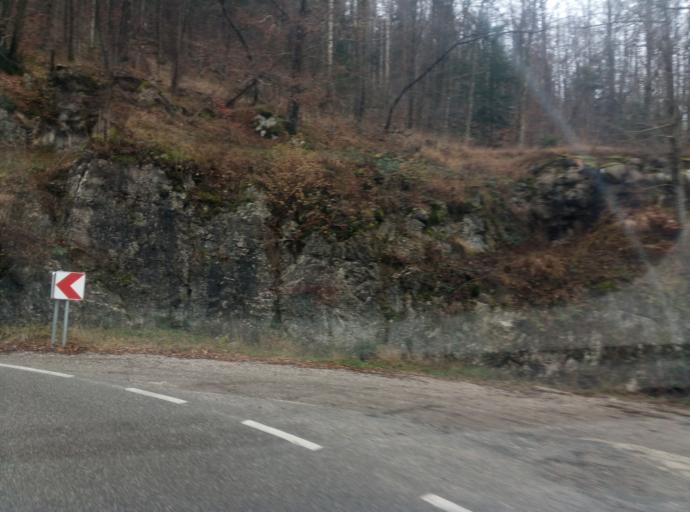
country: SI
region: Idrija
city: Idrija
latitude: 45.9544
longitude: 14.0753
